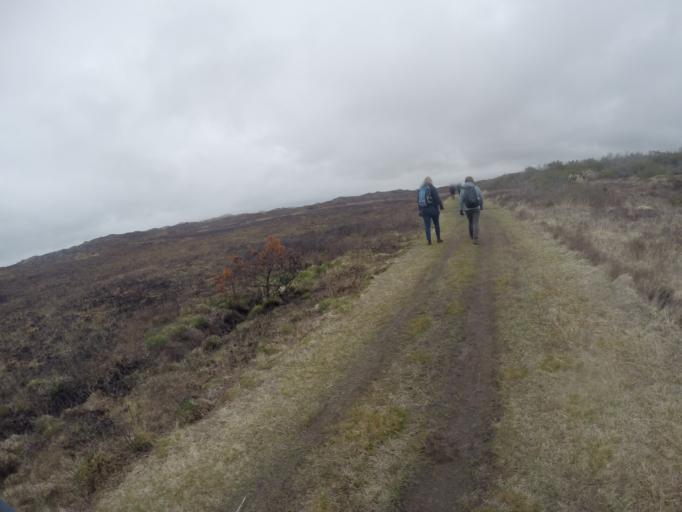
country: DK
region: Central Jutland
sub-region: Lemvig Kommune
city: Thyboron
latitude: 56.8480
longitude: 8.2822
